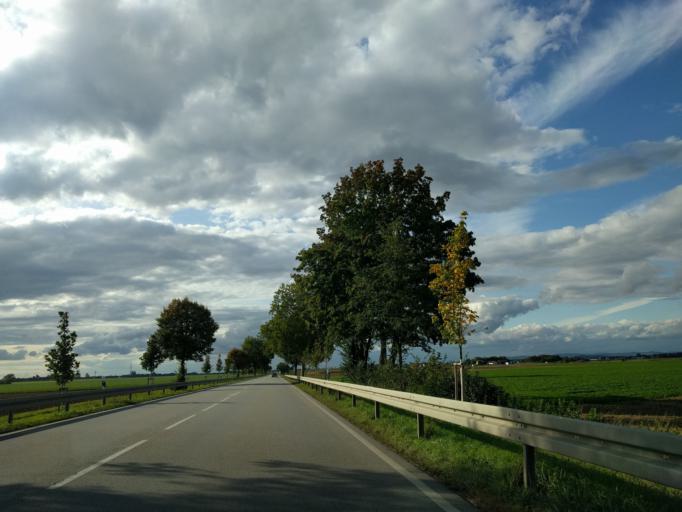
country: DE
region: Bavaria
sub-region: Lower Bavaria
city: Stephansposching
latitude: 48.8023
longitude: 12.7992
